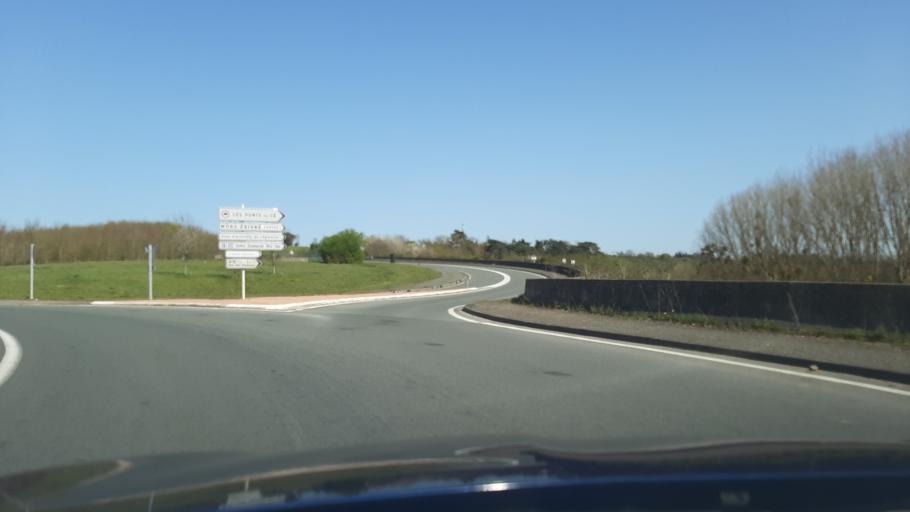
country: FR
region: Pays de la Loire
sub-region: Departement de Maine-et-Loire
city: Murs-Erigne
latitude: 47.3902
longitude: -0.5426
